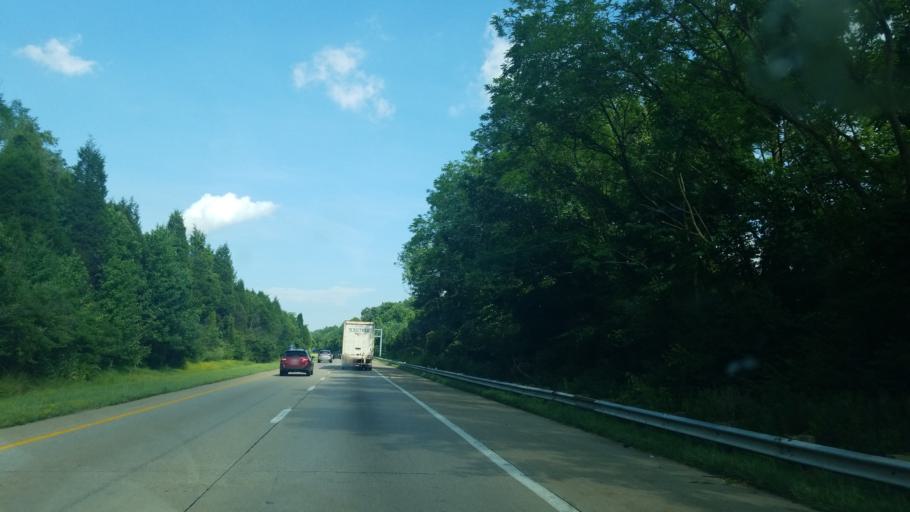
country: US
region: Ohio
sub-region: Hamilton County
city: Salem Heights
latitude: 39.0566
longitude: -84.3800
